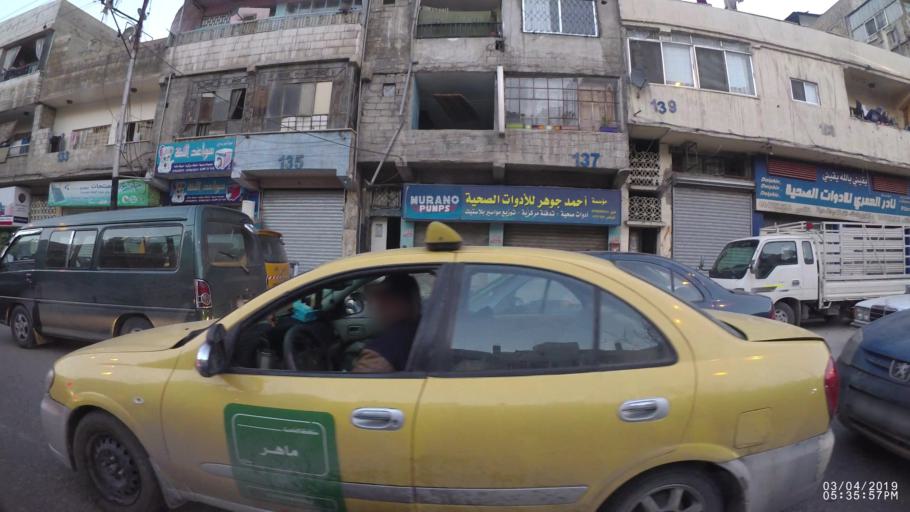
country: JO
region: Amman
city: Amman
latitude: 31.9390
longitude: 35.9236
